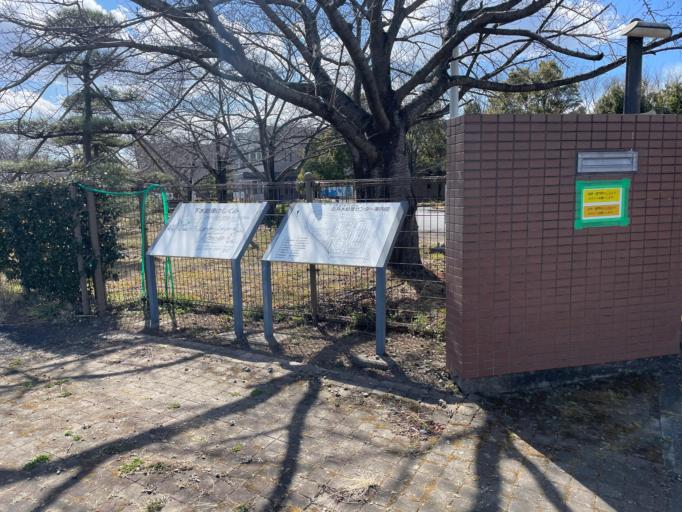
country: JP
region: Saitama
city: Sakado
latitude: 35.9822
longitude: 139.4121
